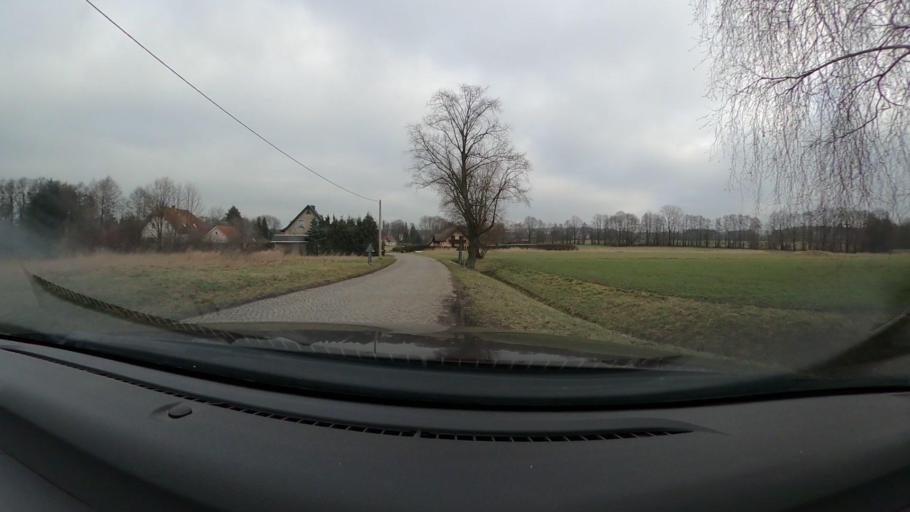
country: DE
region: Saxony
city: Oberschona
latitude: 50.9043
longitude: 13.2834
